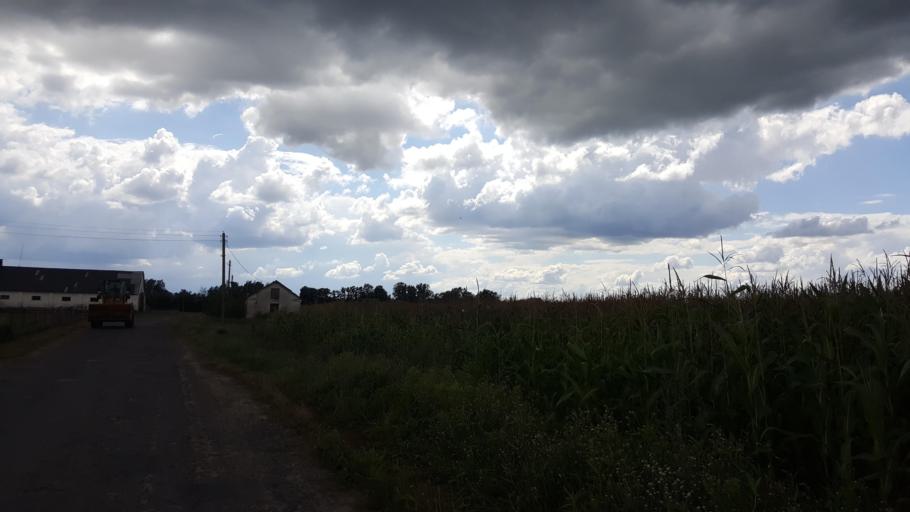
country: BY
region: Brest
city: Zhabinka
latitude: 52.2593
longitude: 23.9683
